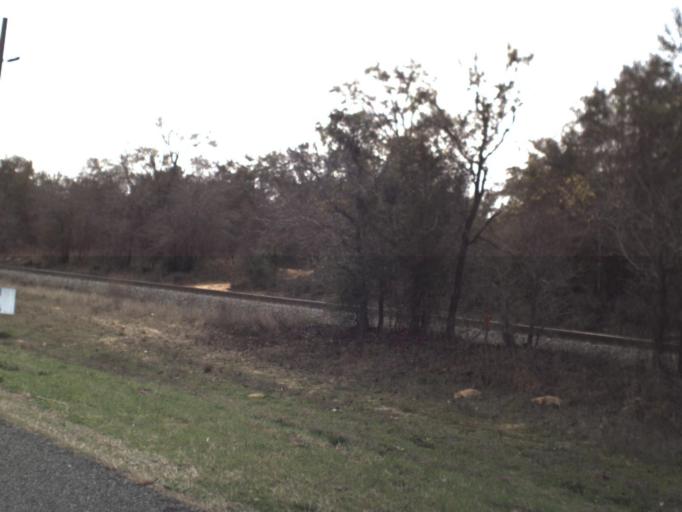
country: US
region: Florida
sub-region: Washington County
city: Chipley
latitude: 30.6430
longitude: -85.4003
